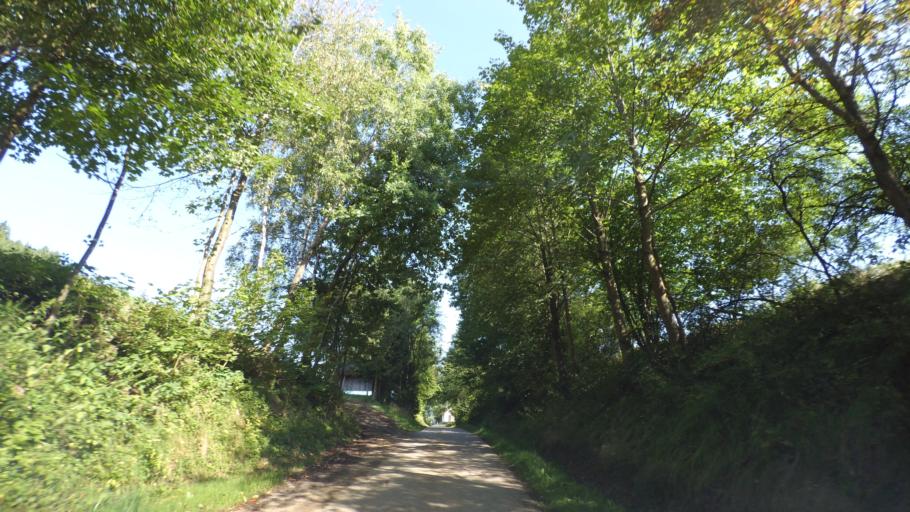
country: DE
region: Bavaria
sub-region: Lower Bavaria
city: Geiersthal
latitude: 49.0601
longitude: 12.9708
